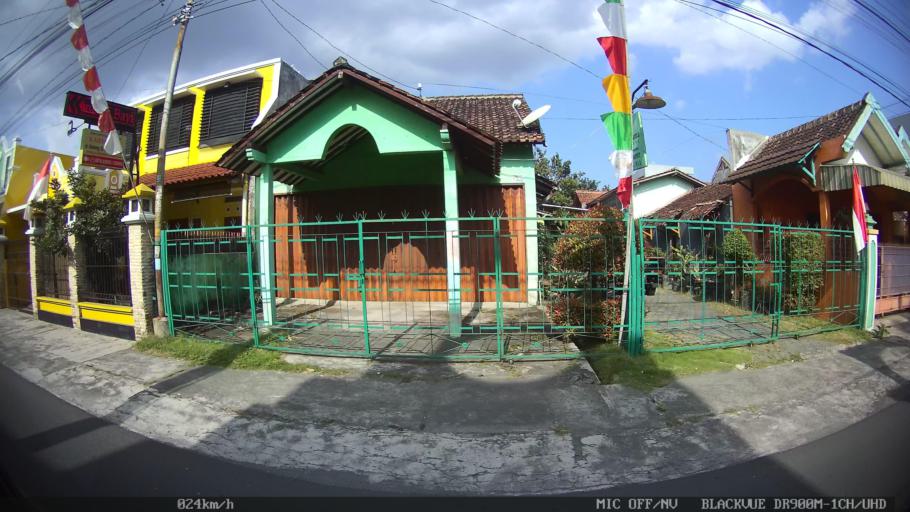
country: ID
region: Daerah Istimewa Yogyakarta
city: Gamping Lor
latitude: -7.7985
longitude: 110.3452
